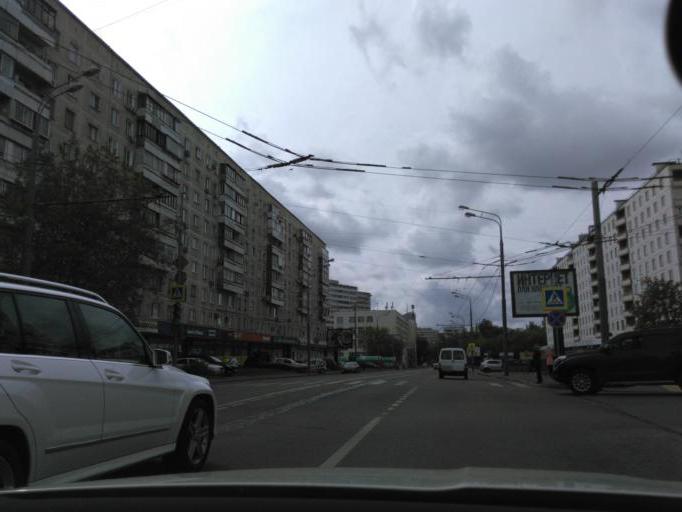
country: RU
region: Moscow
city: Mar'ina Roshcha
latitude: 55.7838
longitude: 37.6418
